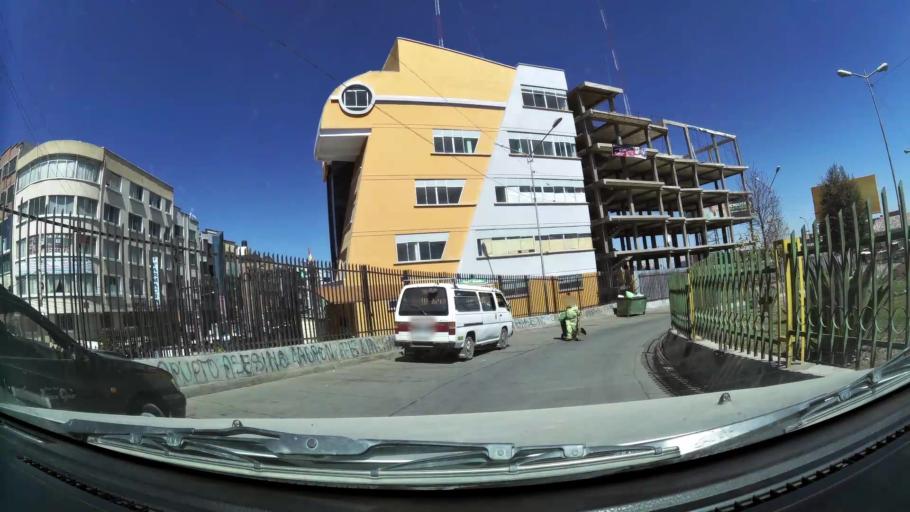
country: BO
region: La Paz
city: La Paz
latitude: -16.5044
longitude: -68.1622
